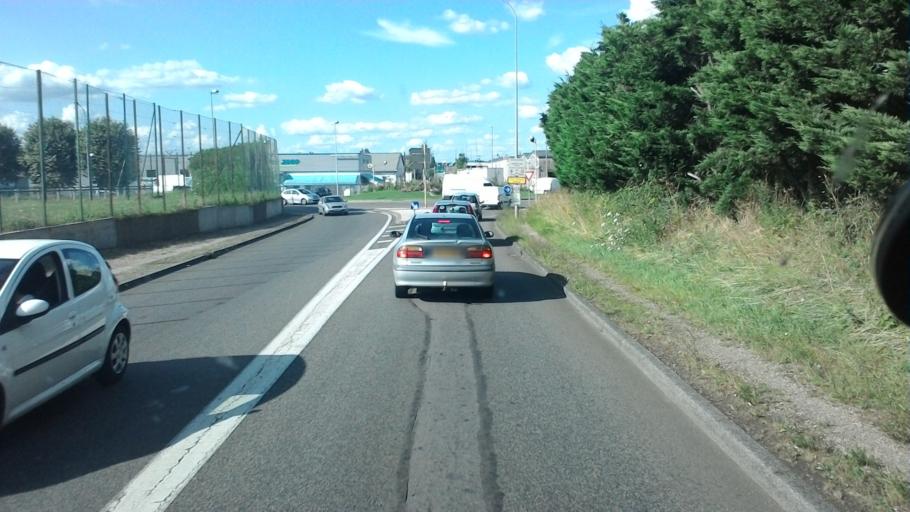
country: FR
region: Franche-Comte
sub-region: Departement de la Haute-Saone
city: Noidans-les-Vesoul
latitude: 47.6164
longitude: 6.1339
